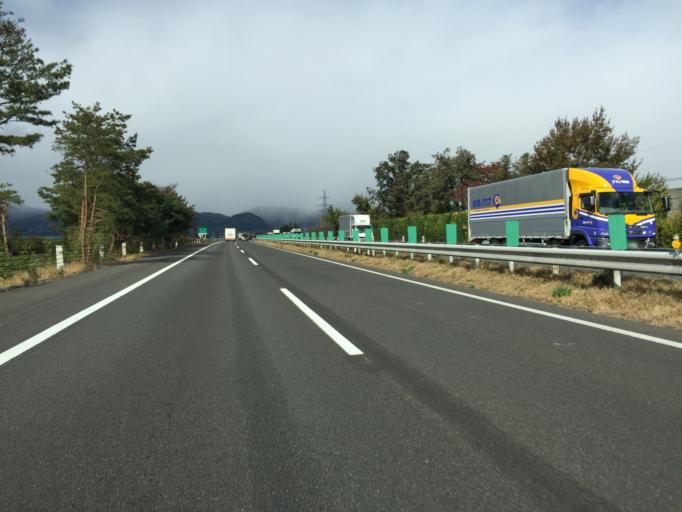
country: JP
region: Fukushima
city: Fukushima-shi
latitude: 37.7469
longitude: 140.4131
